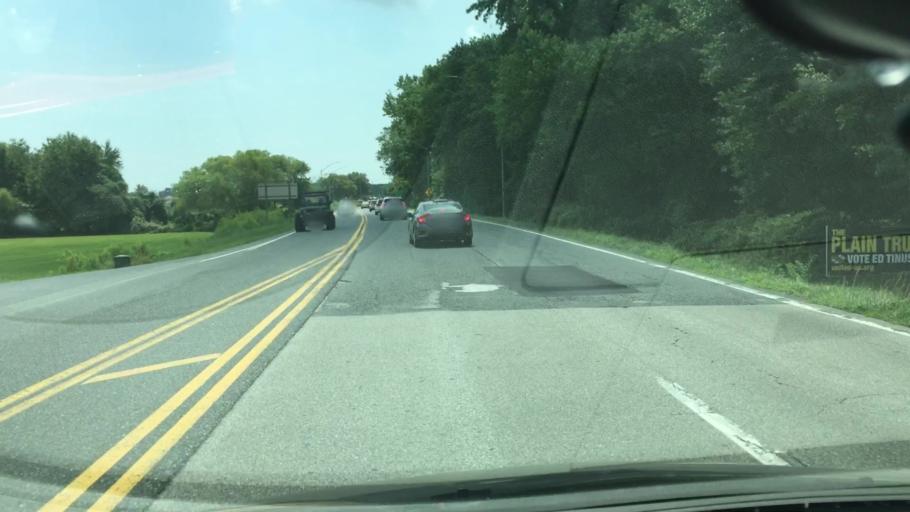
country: US
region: Maryland
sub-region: Worcester County
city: Ocean Pines
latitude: 38.3504
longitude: -75.1683
